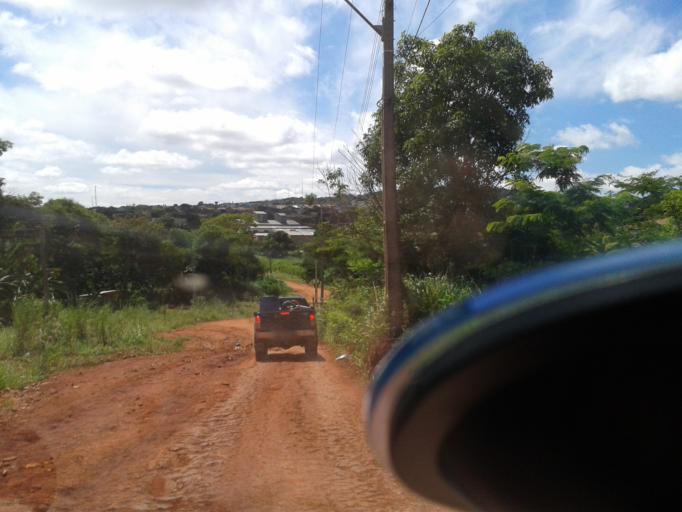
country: BR
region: Goias
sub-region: Goiania
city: Goiania
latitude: -16.6485
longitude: -49.3551
